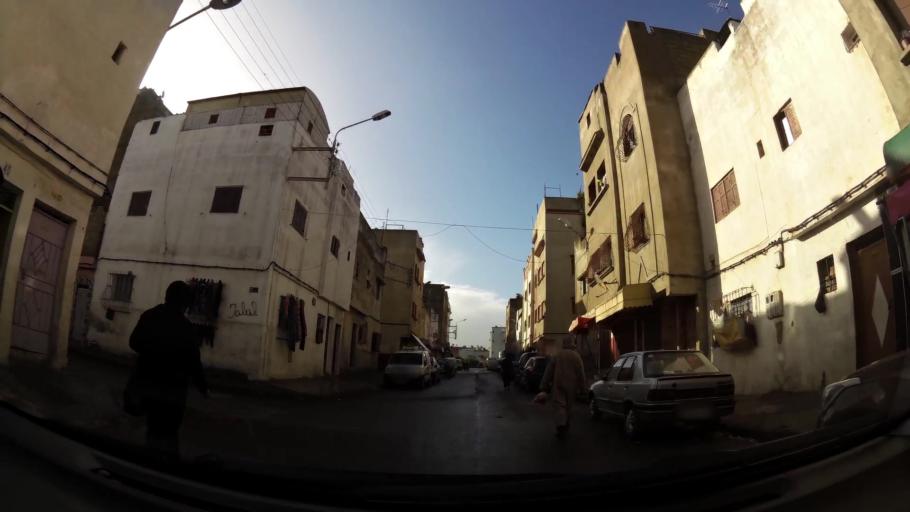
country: MA
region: Grand Casablanca
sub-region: Casablanca
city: Casablanca
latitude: 33.5553
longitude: -7.6877
